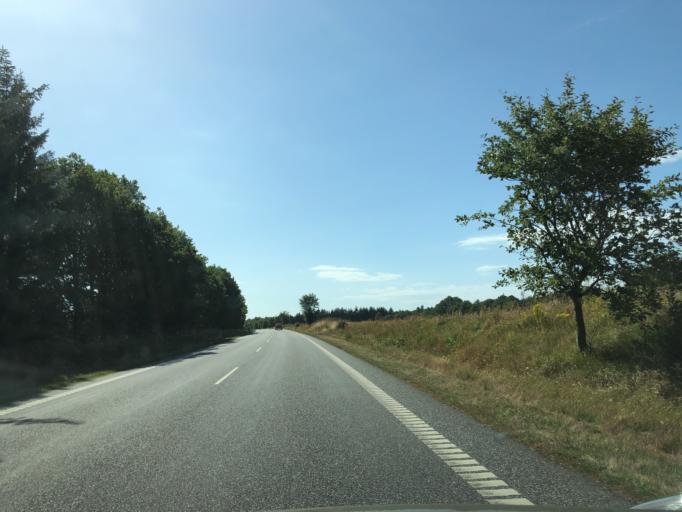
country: DK
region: North Denmark
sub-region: Vesthimmerland Kommune
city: Alestrup
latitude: 56.6122
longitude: 9.3874
